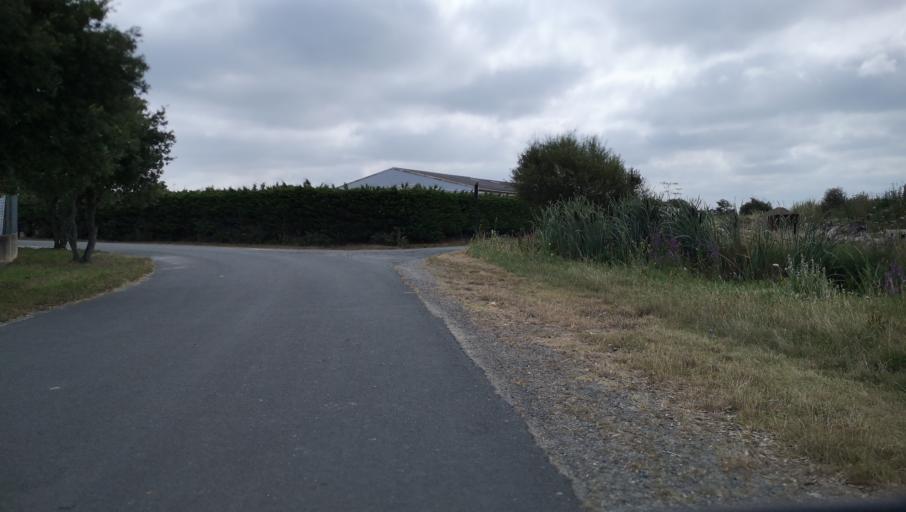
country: FR
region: Pays de la Loire
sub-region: Departement de la Vendee
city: Bretignolles-sur-Mer
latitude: 46.5965
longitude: -1.8275
